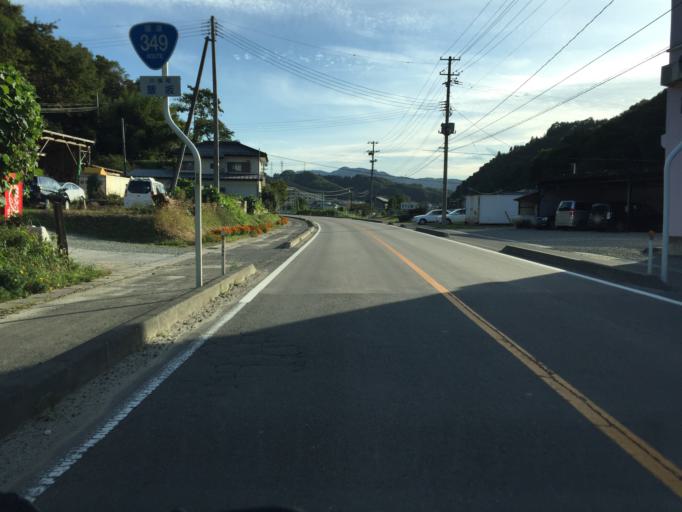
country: JP
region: Fukushima
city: Hobaramachi
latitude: 37.6749
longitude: 140.6140
